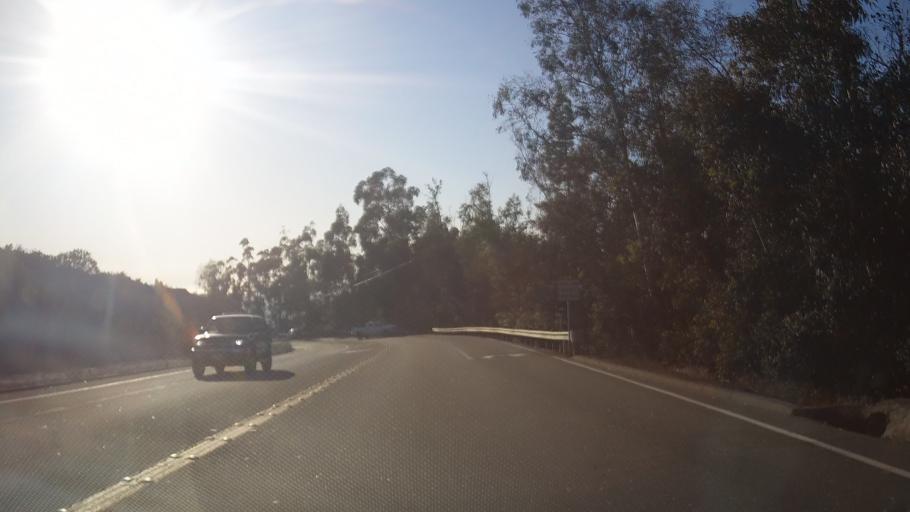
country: US
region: California
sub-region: San Diego County
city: Poway
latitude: 32.9787
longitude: -116.9858
